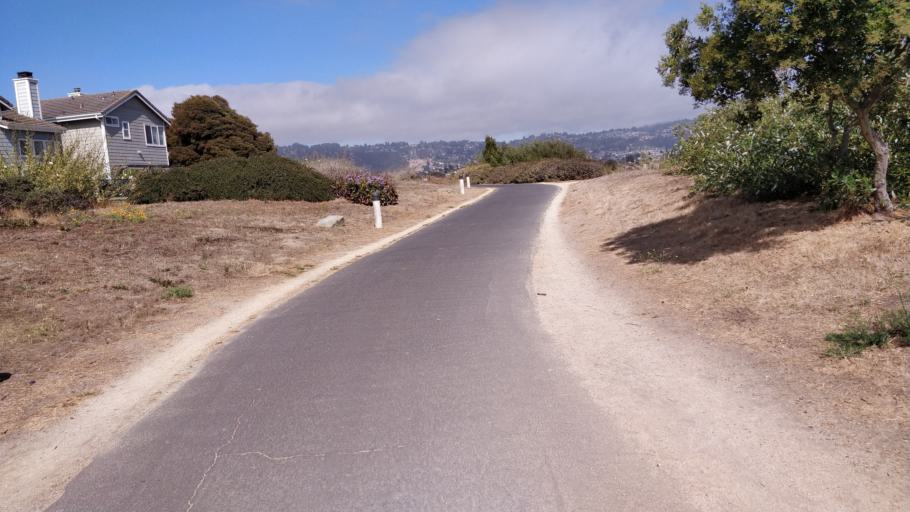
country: US
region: California
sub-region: Contra Costa County
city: Richmond
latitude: 37.9103
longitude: -122.3390
